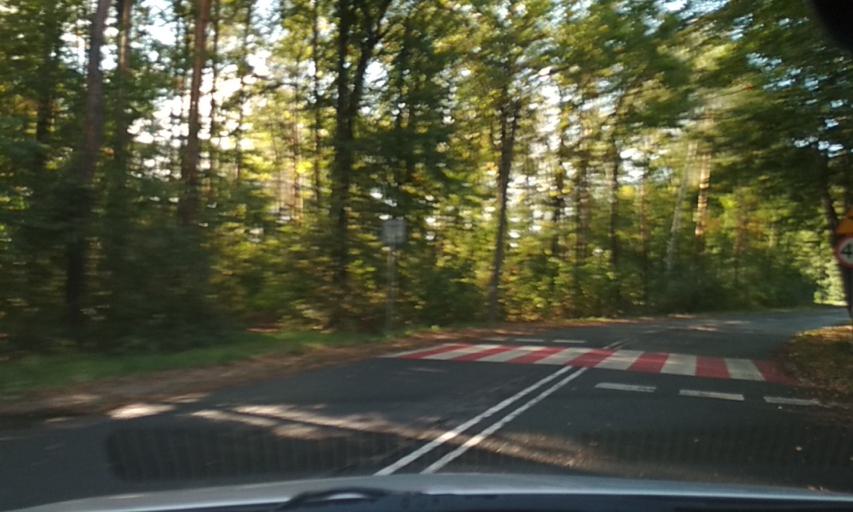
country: PL
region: Silesian Voivodeship
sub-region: Powiat bierunsko-ledzinski
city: Ledziny
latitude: 50.1703
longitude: 19.1568
